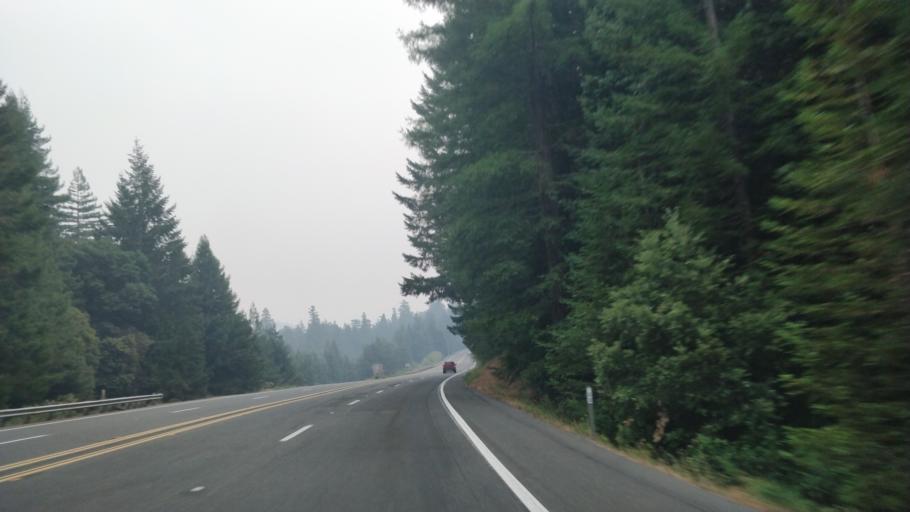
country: US
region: California
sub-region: Humboldt County
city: Rio Dell
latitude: 40.3865
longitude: -123.9301
